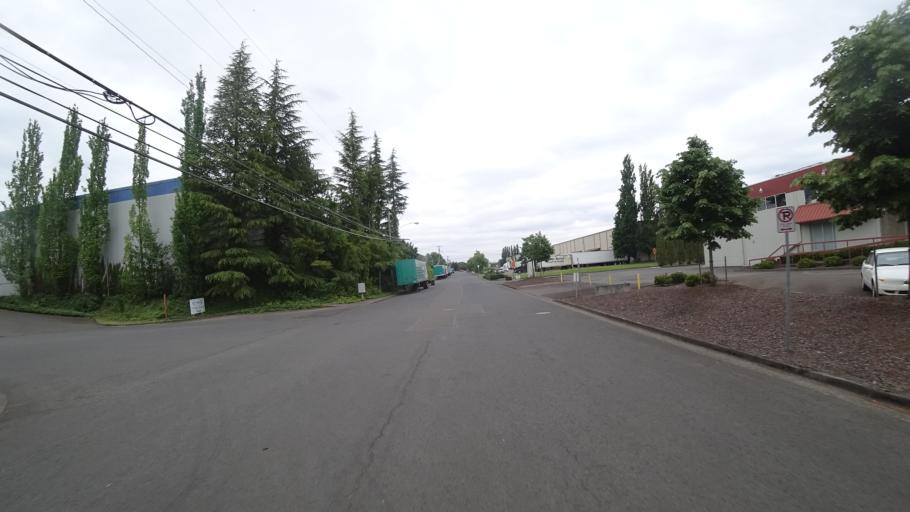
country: US
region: Oregon
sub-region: Washington County
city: Beaverton
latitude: 45.4801
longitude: -122.7874
